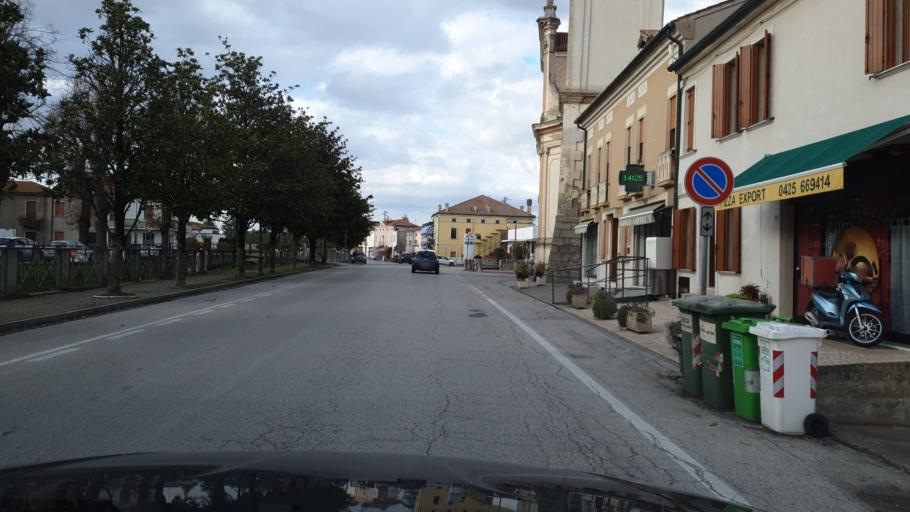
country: IT
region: Veneto
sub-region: Provincia di Rovigo
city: Villanova del Ghebbo Canton
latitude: 45.0553
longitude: 11.6446
